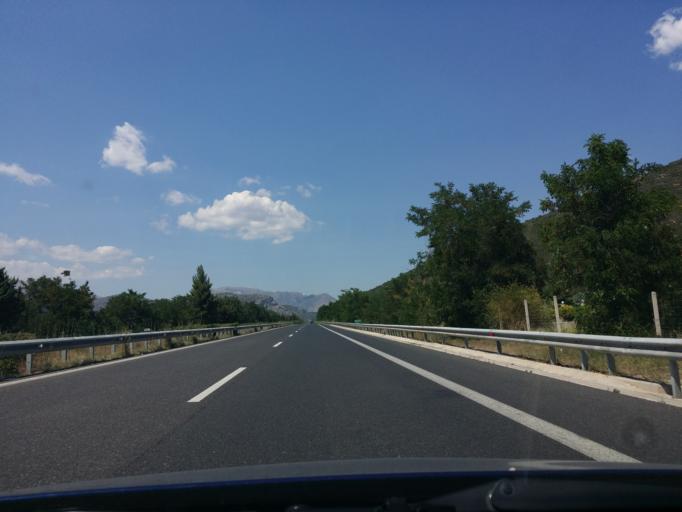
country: GR
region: Peloponnese
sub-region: Nomos Arkadias
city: Tripoli
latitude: 37.5603
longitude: 22.4237
